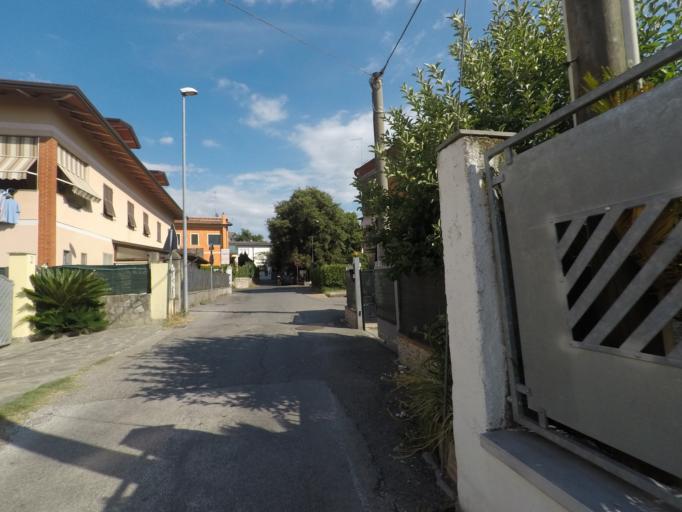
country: IT
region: Tuscany
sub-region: Provincia di Massa-Carrara
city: Massa
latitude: 44.0197
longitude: 10.1215
